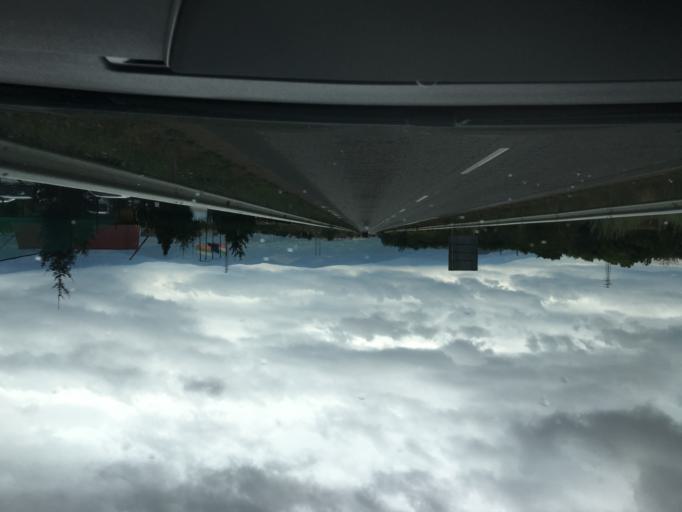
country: BG
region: Kyustendil
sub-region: Obshtina Kyustendil
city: Kyustendil
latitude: 42.2841
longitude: 22.7200
